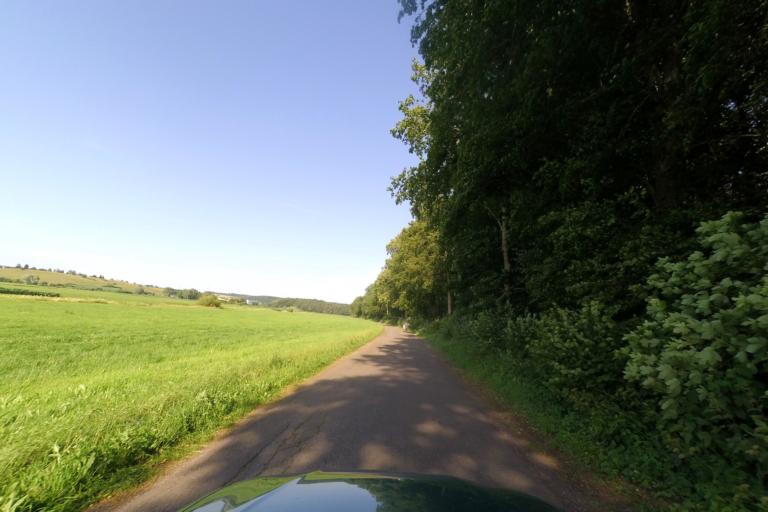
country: DE
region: Baden-Wuerttemberg
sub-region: Regierungsbezirk Stuttgart
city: Hermaringen
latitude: 48.5813
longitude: 10.2502
